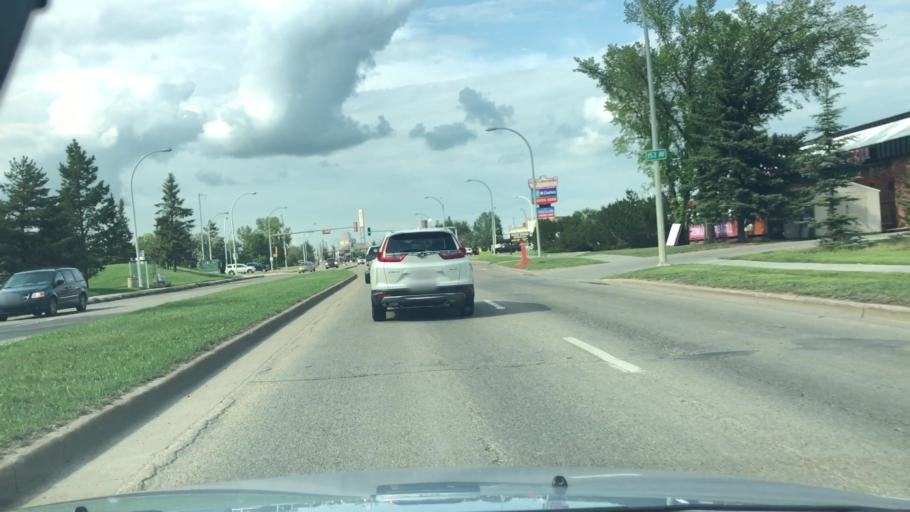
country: CA
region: Alberta
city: Edmonton
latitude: 53.6128
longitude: -113.5166
